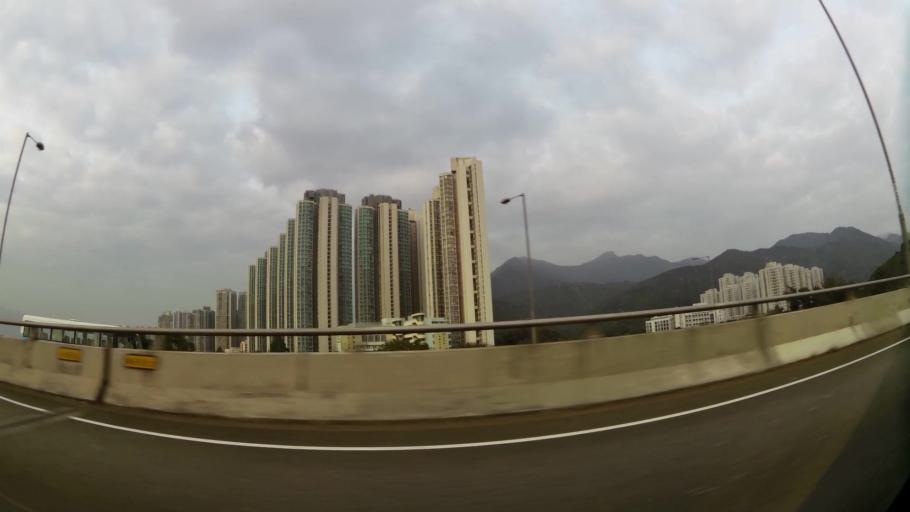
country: HK
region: Sha Tin
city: Sha Tin
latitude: 22.4056
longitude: 114.2183
